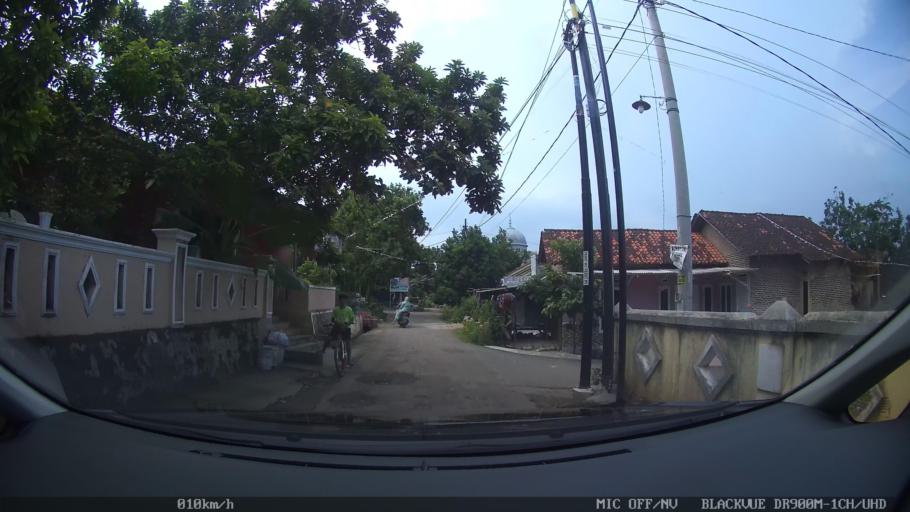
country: ID
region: Lampung
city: Kedaton
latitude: -5.3870
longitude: 105.2131
